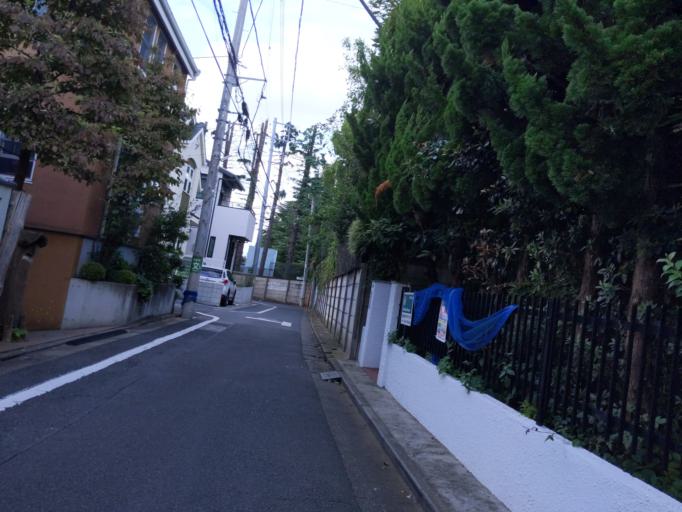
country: JP
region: Saitama
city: Wako
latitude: 35.7433
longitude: 139.6424
